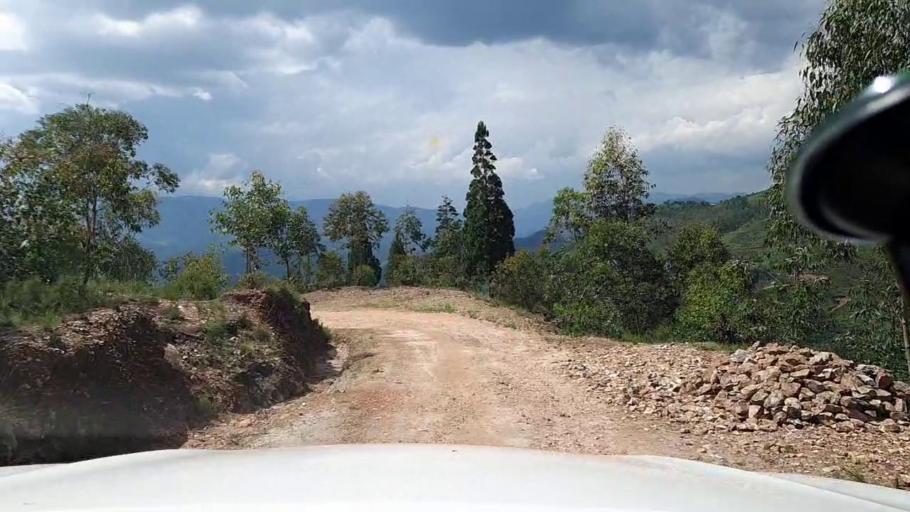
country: RW
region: Southern Province
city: Gitarama
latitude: -1.8399
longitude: 29.8193
